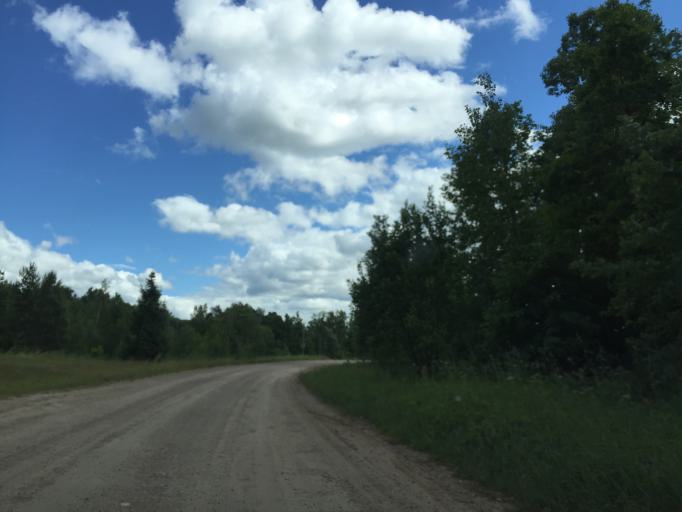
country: LV
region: Vecumnieki
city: Vecumnieki
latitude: 56.5032
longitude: 24.4045
